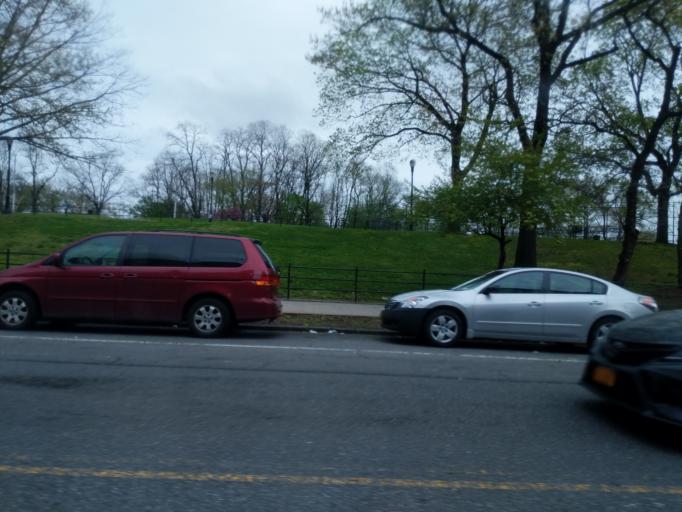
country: US
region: New York
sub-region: New York County
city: Inwood
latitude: 40.8420
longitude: -73.9354
